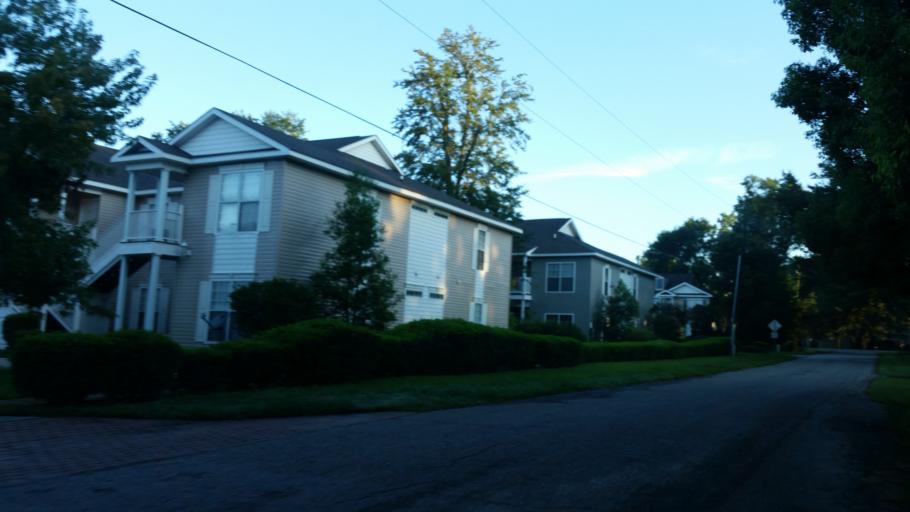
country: US
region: Florida
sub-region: Escambia County
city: Ferry Pass
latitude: 30.4983
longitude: -87.2174
